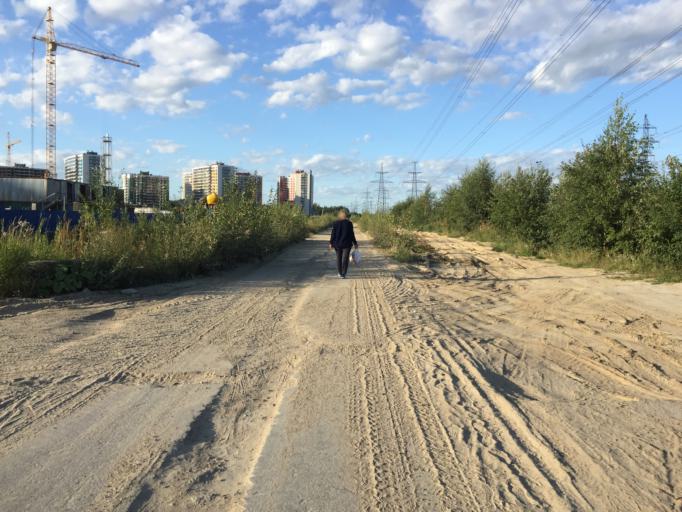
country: RU
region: Leningrad
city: Murino
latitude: 60.0639
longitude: 30.4475
